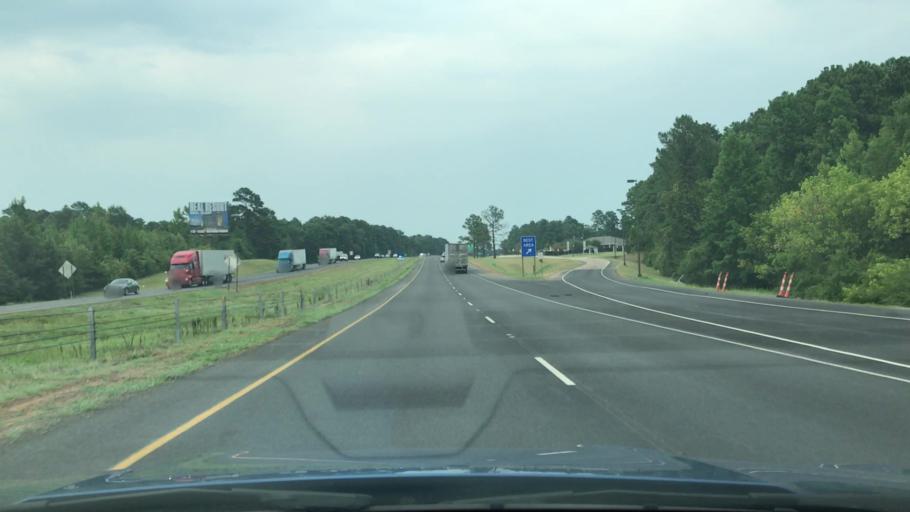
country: US
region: Louisiana
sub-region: Caddo Parish
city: Greenwood
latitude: 32.4516
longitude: -94.0059
